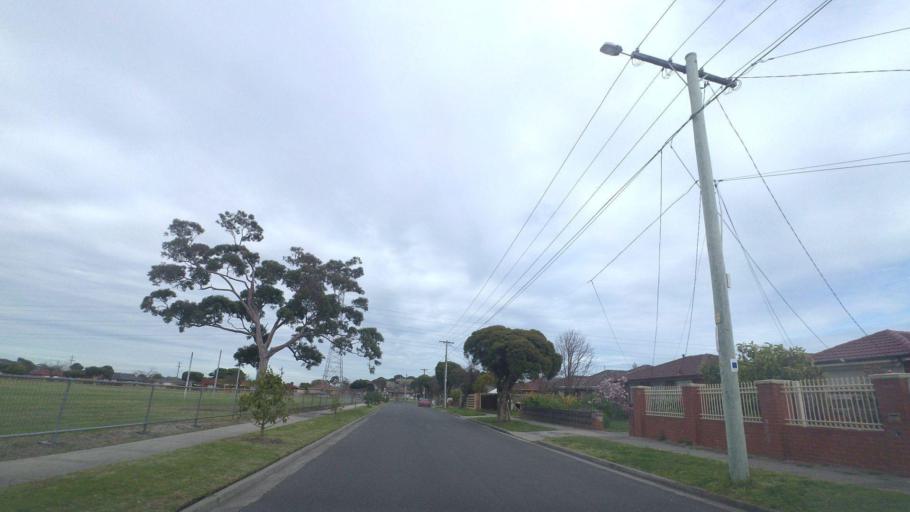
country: AU
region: Victoria
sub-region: Kingston
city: Clayton South
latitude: -37.9410
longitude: 145.1340
